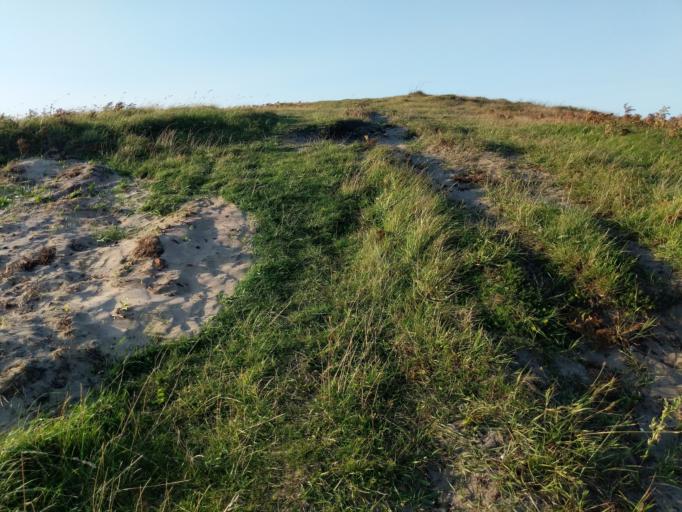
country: GB
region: England
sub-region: Northumberland
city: Lynemouth
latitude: 55.2160
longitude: -1.5283
